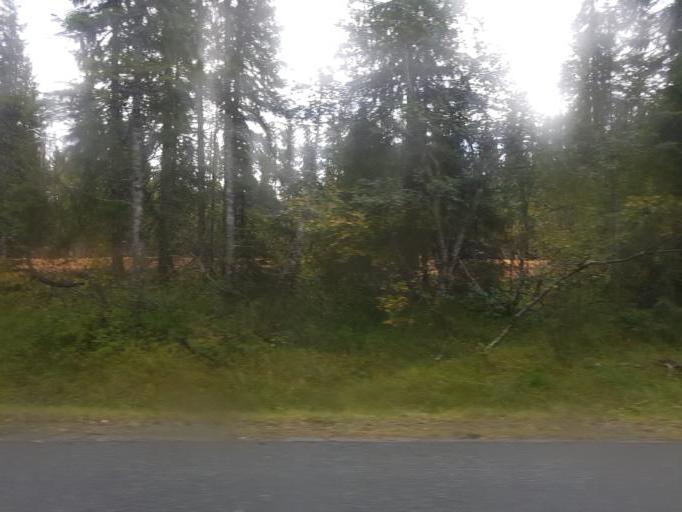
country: NO
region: Sor-Trondelag
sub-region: Trondheim
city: Trondheim
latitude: 63.4167
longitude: 10.2906
